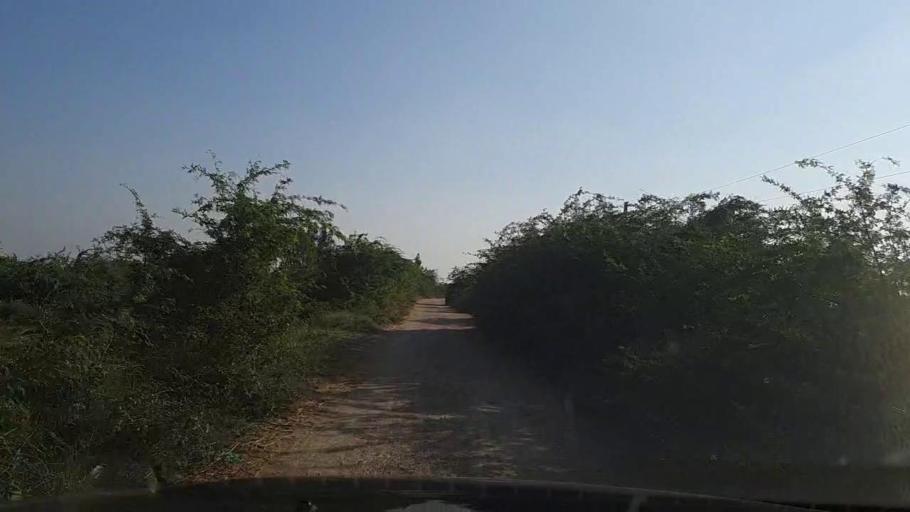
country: PK
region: Sindh
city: Gharo
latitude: 24.7115
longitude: 67.7038
